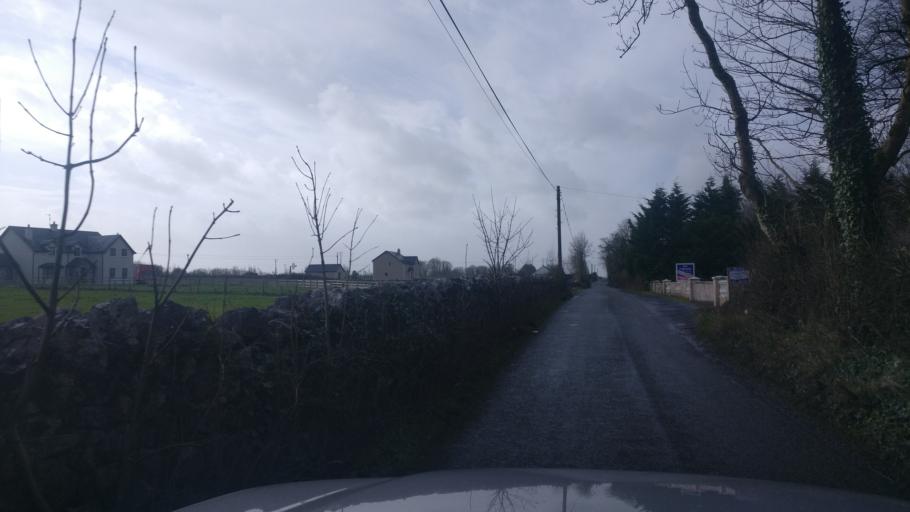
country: IE
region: Connaught
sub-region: County Galway
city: Loughrea
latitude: 53.2698
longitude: -8.5970
